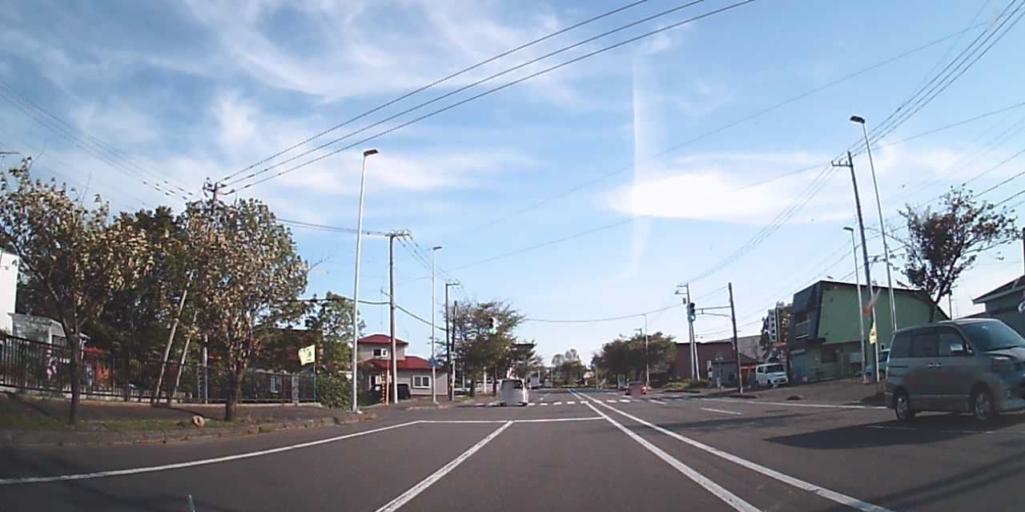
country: JP
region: Hokkaido
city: Shiraoi
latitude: 42.4573
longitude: 141.1773
